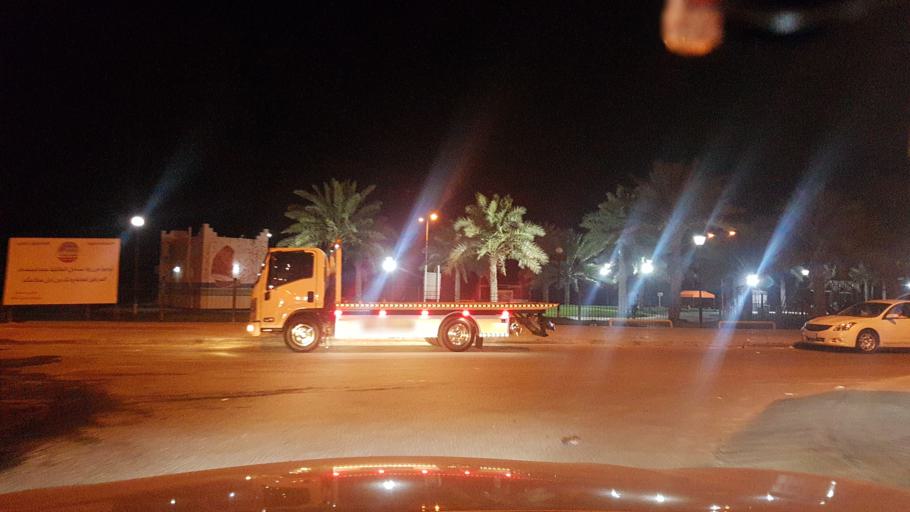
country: BH
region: Central Governorate
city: Madinat Hamad
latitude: 26.0943
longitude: 50.4797
